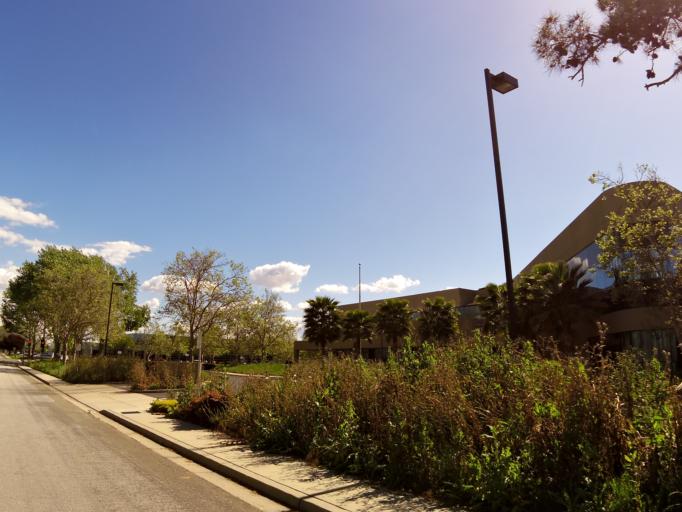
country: US
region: California
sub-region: Santa Clara County
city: Milpitas
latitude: 37.4770
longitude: -121.9387
